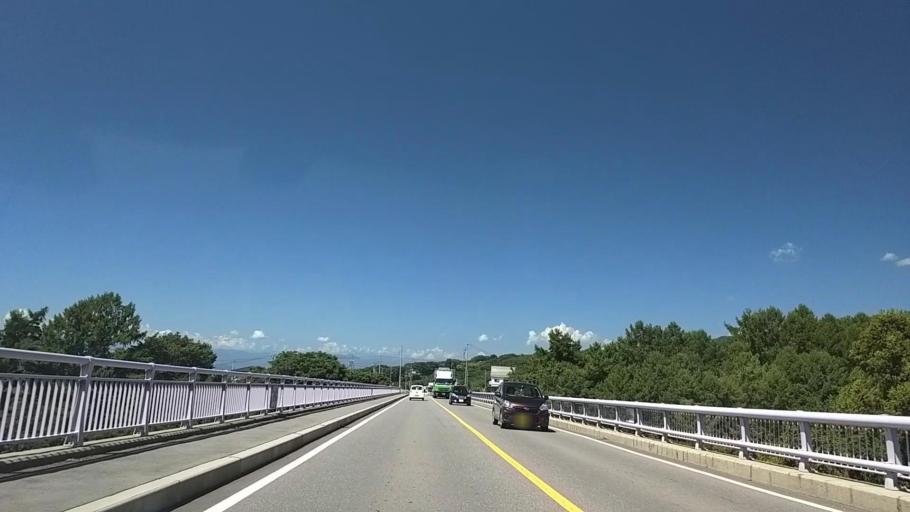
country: JP
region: Nagano
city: Komoro
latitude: 36.3455
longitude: 138.4367
